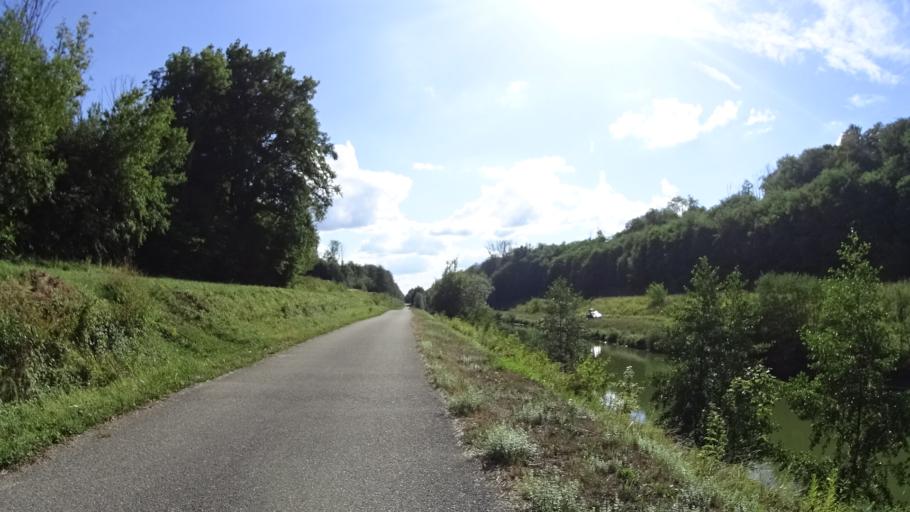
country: FR
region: Franche-Comte
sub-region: Territoire de Belfort
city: Montreux-Chateau
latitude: 47.6296
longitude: 7.0543
